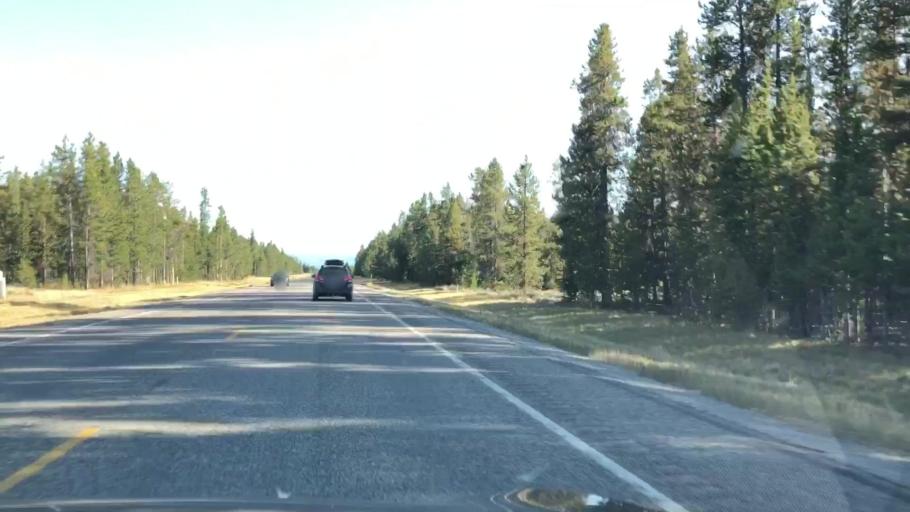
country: US
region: Montana
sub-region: Gallatin County
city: West Yellowstone
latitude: 44.7282
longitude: -111.1078
